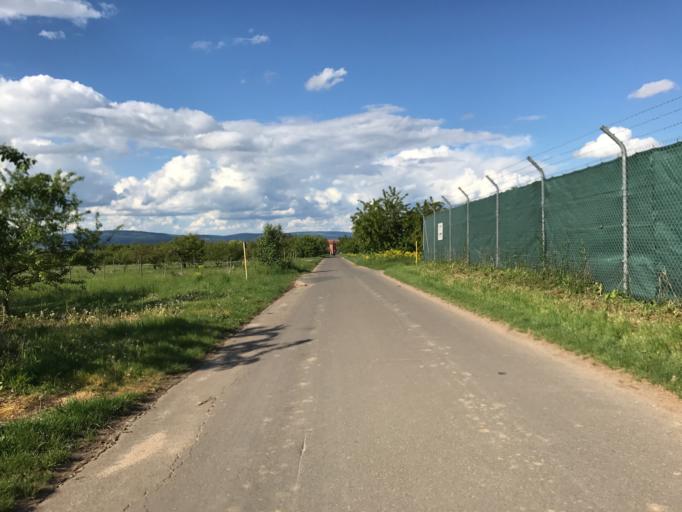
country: DE
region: Rheinland-Pfalz
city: Wackernheim
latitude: 49.9705
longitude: 8.1140
